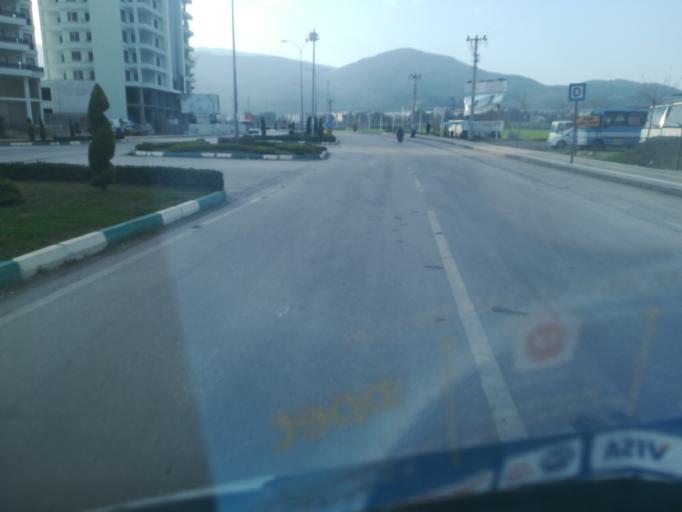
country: TR
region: Osmaniye
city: Osmaniye
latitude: 37.0543
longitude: 36.2225
